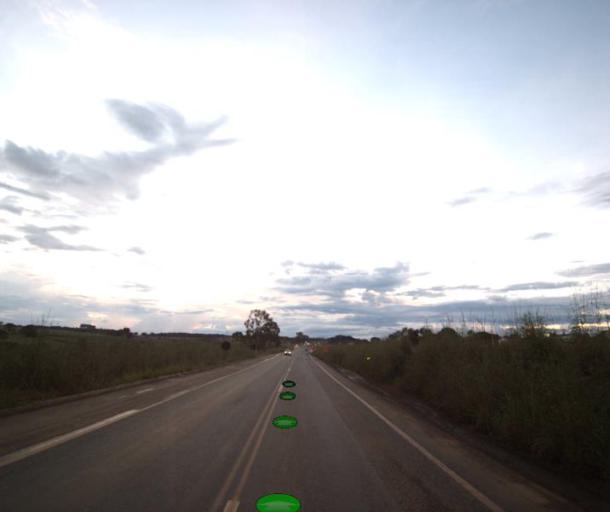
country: BR
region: Goias
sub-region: Anapolis
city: Anapolis
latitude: -16.1936
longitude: -49.0294
